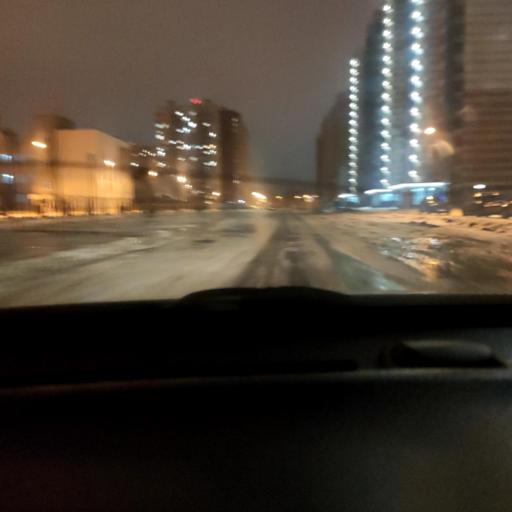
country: RU
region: Voronezj
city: Voronezh
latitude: 51.7137
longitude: 39.2636
